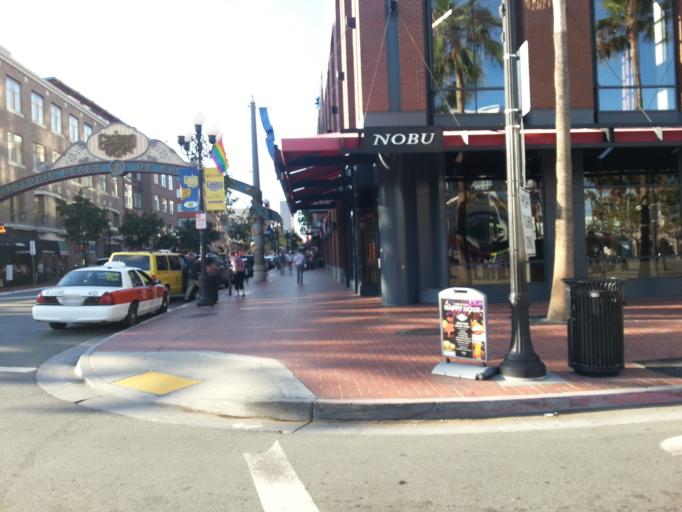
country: US
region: California
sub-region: San Diego County
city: San Diego
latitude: 32.7074
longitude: -117.1601
